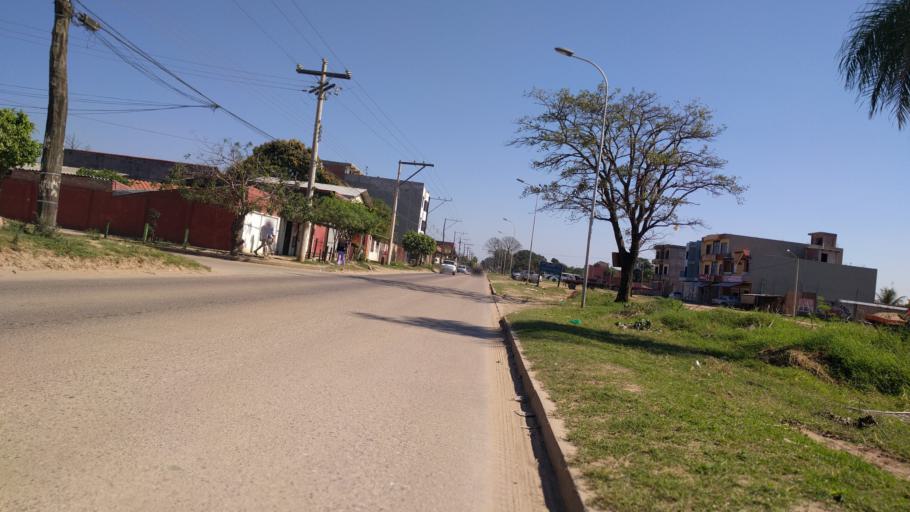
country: BO
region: Santa Cruz
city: Santa Cruz de la Sierra
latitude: -17.8508
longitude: -63.2014
